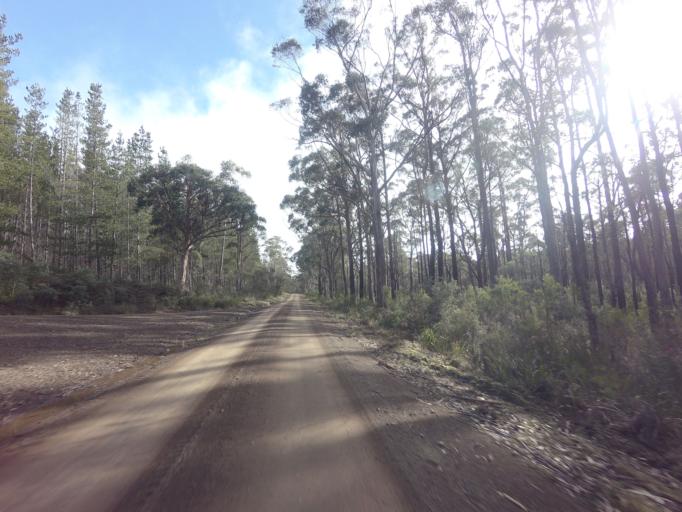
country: AU
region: Tasmania
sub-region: Derwent Valley
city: New Norfolk
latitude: -42.7633
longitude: 146.8966
